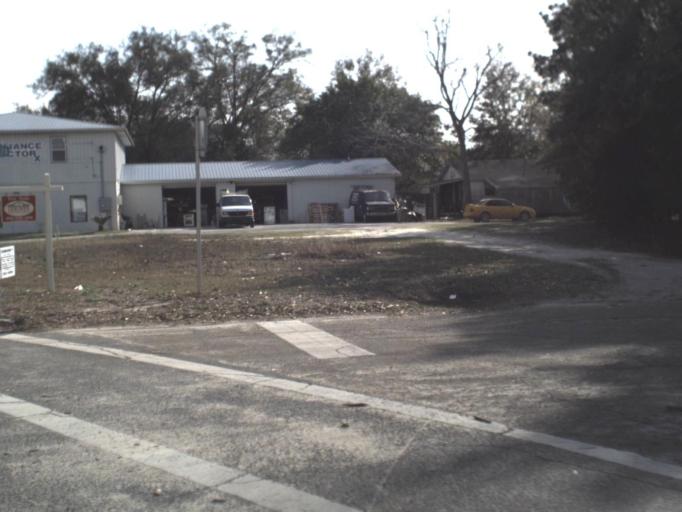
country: US
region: Florida
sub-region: Bay County
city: Springfield
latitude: 30.1523
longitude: -85.6167
